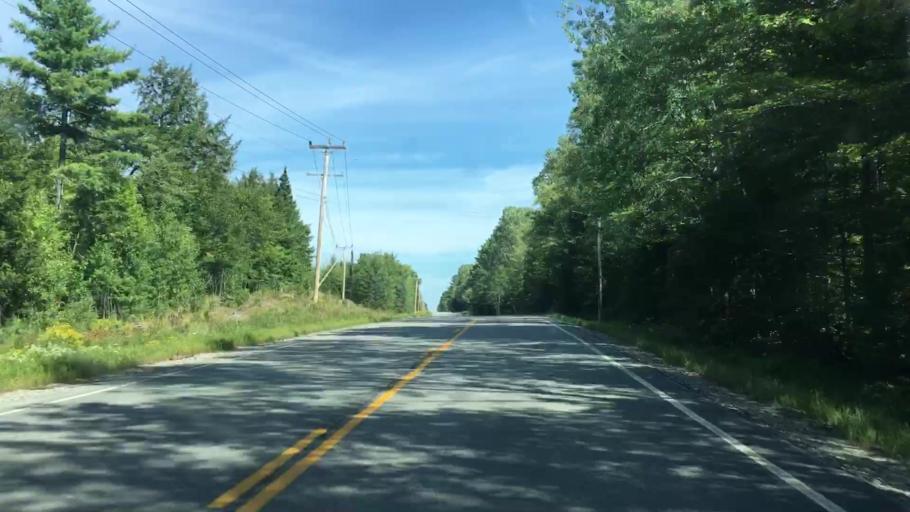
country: US
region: Maine
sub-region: Penobscot County
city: Howland
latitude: 45.2313
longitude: -68.7011
